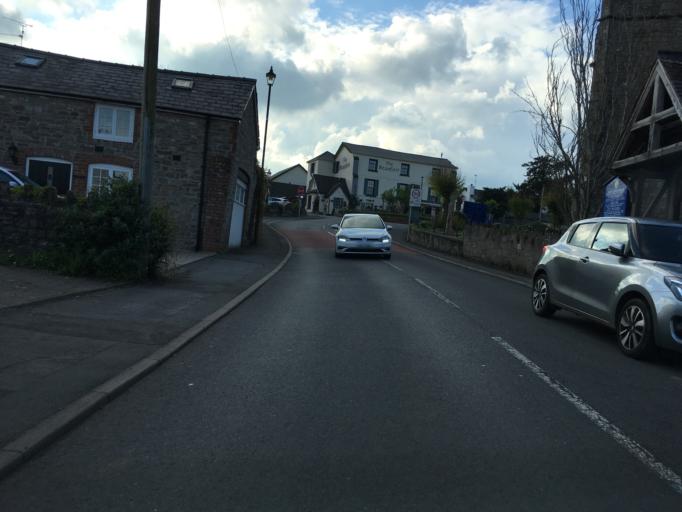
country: GB
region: Wales
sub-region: Monmouthshire
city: Llanarth
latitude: 51.7644
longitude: -2.8515
